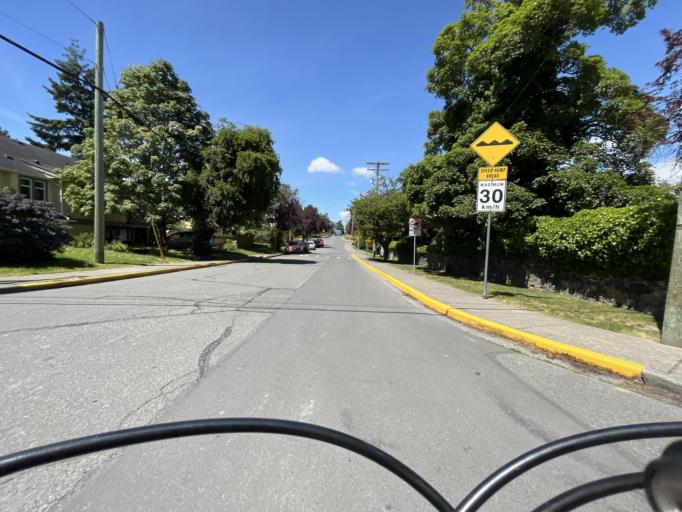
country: CA
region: British Columbia
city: Victoria
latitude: 48.4413
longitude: -123.3933
